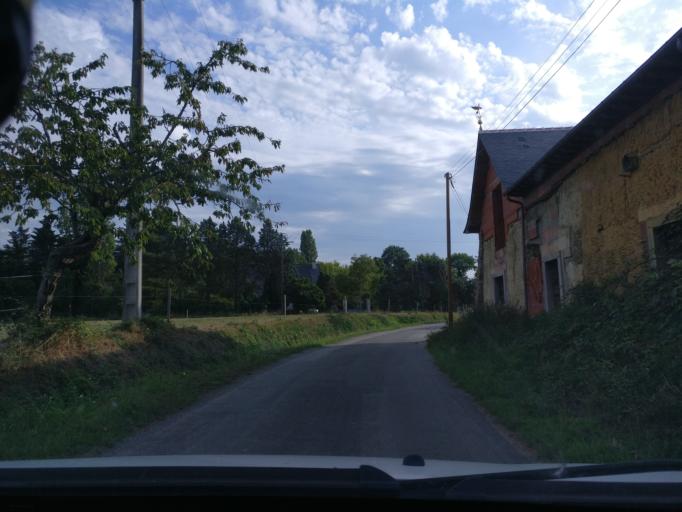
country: FR
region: Brittany
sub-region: Departement d'Ille-et-Vilaine
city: Fouillard
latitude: 48.1320
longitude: -1.5785
